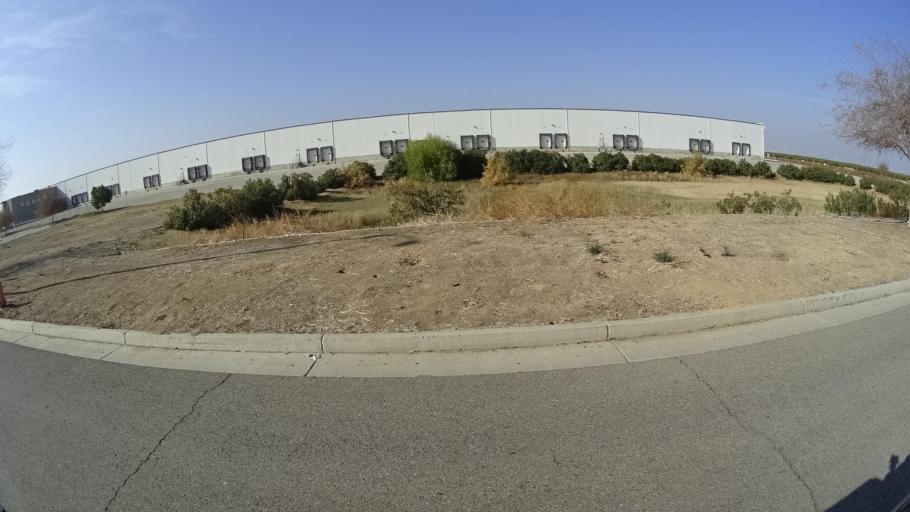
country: US
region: California
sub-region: Kern County
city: Delano
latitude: 35.7313
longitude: -119.2238
